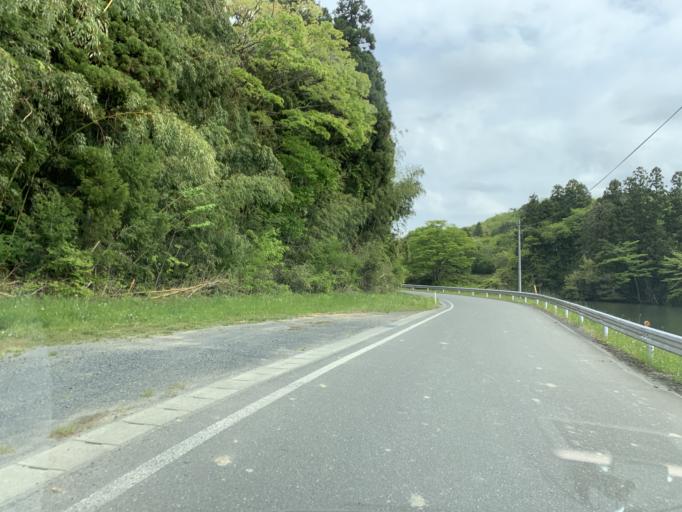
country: JP
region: Iwate
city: Ichinoseki
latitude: 38.8538
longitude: 141.1965
